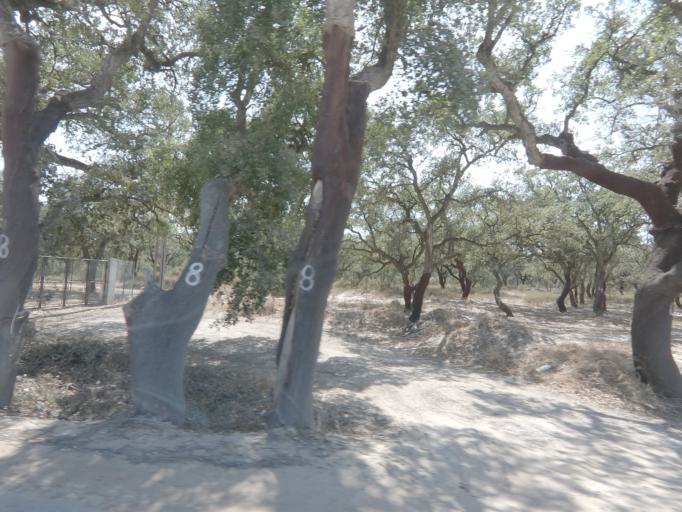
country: PT
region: Setubal
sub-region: Palmela
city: Palmela
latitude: 38.5929
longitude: -8.8552
